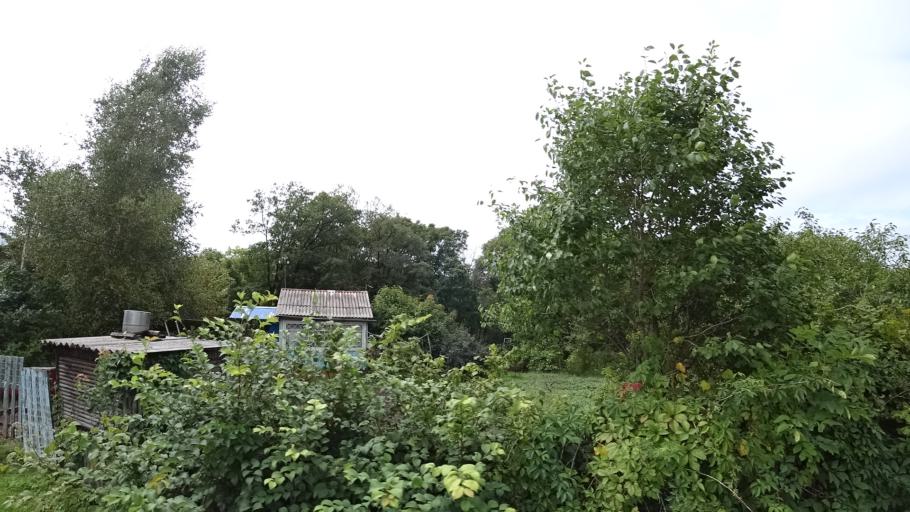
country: RU
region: Primorskiy
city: Monastyrishche
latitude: 44.1666
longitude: 132.5412
